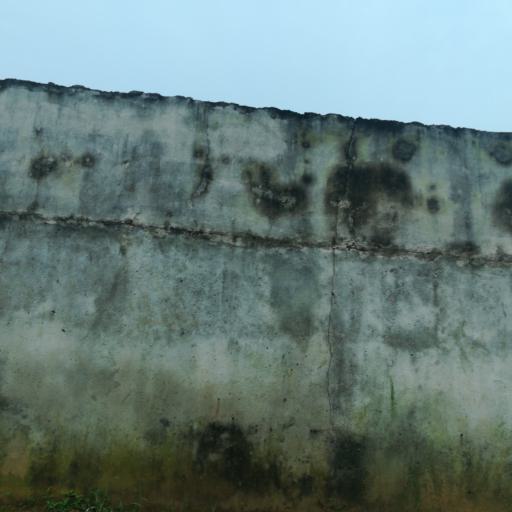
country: NG
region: Rivers
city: Port Harcourt
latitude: 4.7475
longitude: 7.0063
